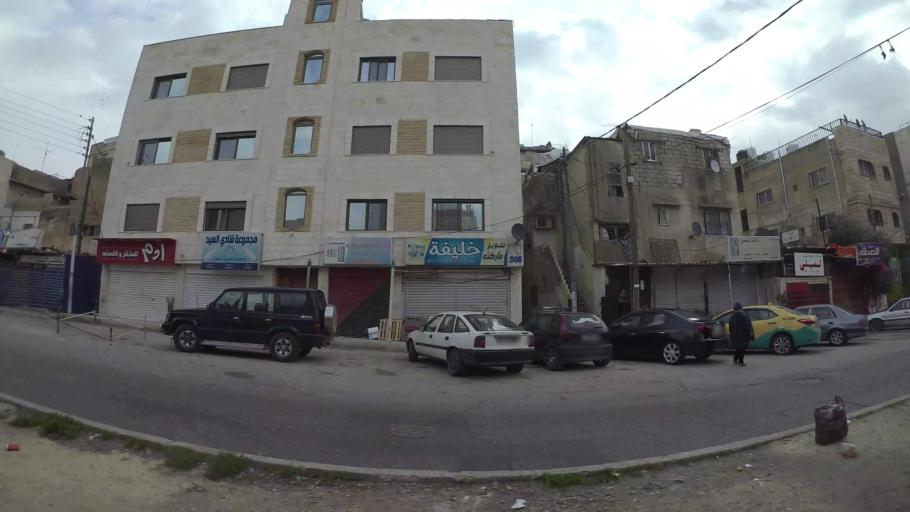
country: JO
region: Amman
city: Amman
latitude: 31.9666
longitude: 35.9266
